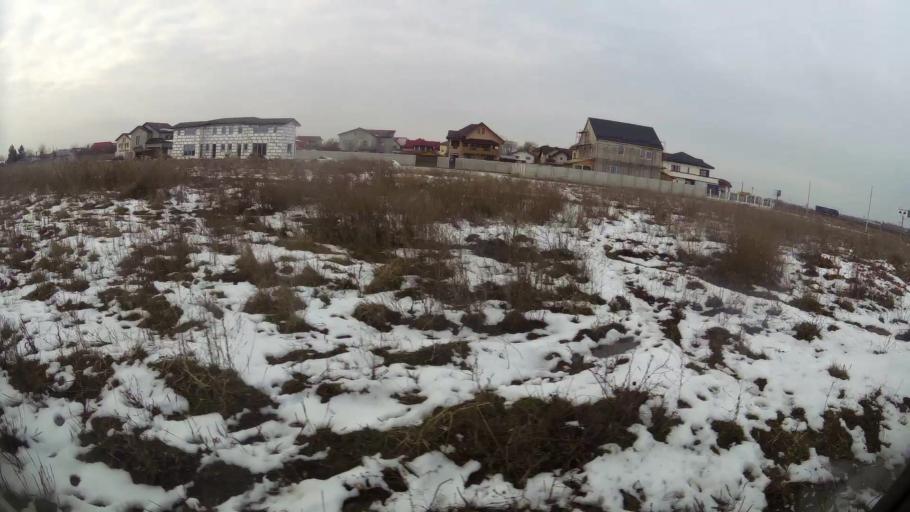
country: RO
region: Ilfov
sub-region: Comuna Glina
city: Catelu
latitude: 44.4040
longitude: 26.2273
